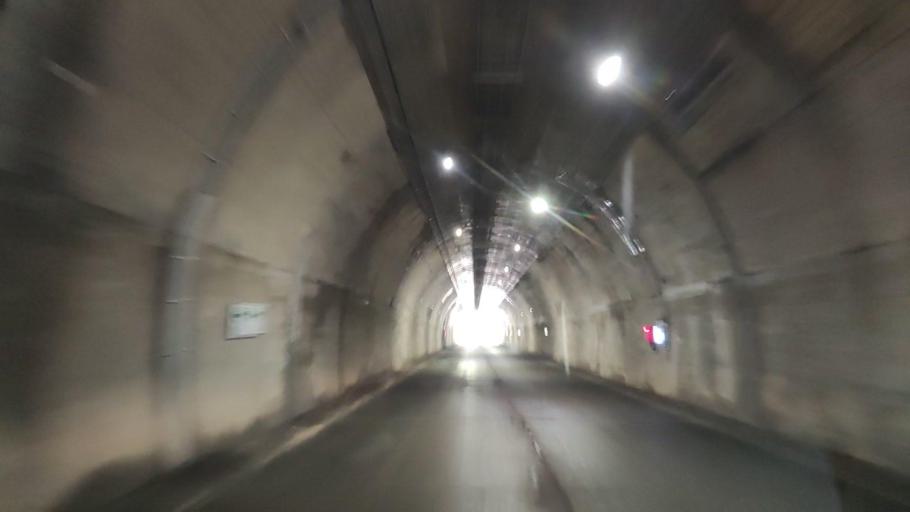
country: JP
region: Yamagata
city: Shinjo
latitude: 38.9601
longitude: 140.3573
